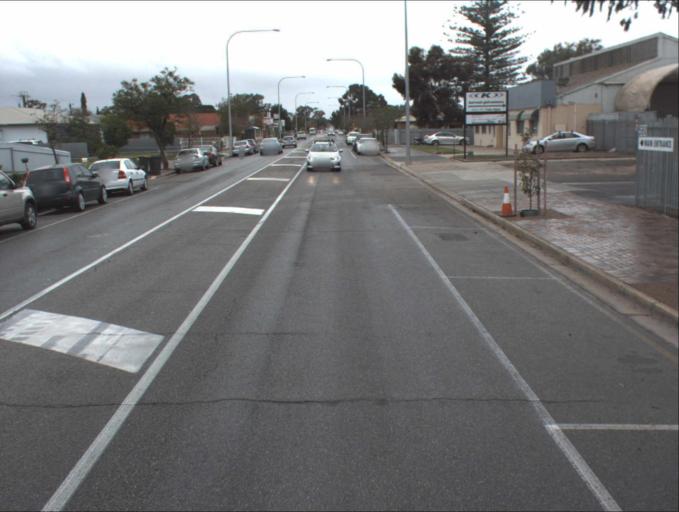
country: AU
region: South Australia
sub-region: Port Adelaide Enfield
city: Blair Athol
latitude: -34.8514
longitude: 138.5916
